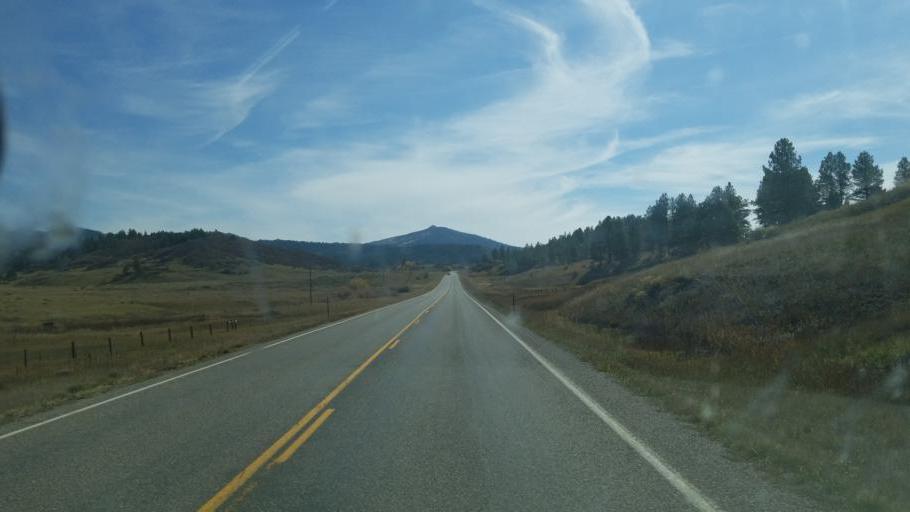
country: US
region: New Mexico
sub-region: Rio Arriba County
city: Dulce
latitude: 37.0111
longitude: -106.8022
